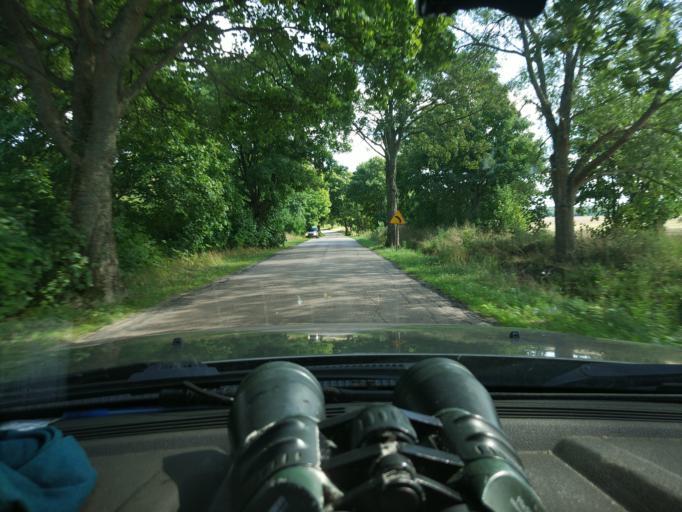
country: PL
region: Pomeranian Voivodeship
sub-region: Powiat wejherowski
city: Choczewo
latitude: 54.7415
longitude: 17.8140
